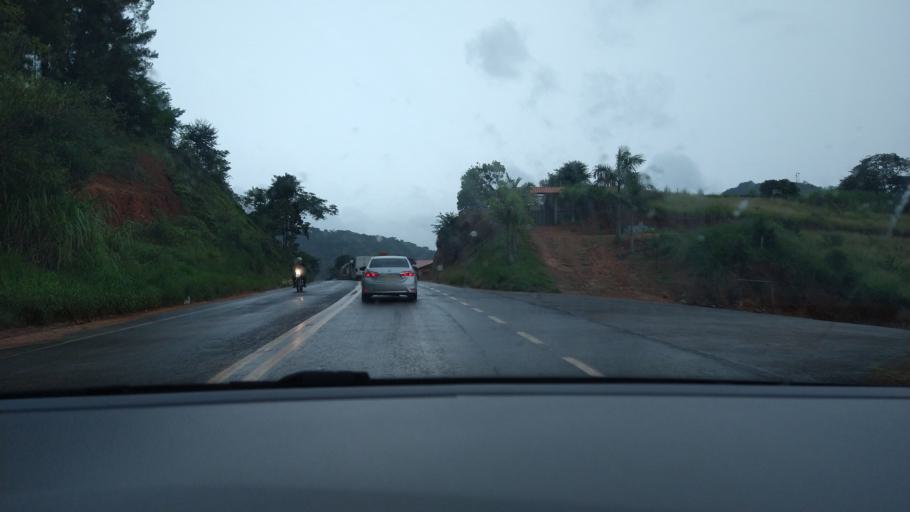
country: BR
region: Minas Gerais
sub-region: Vicosa
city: Vicosa
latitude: -20.6467
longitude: -42.8657
